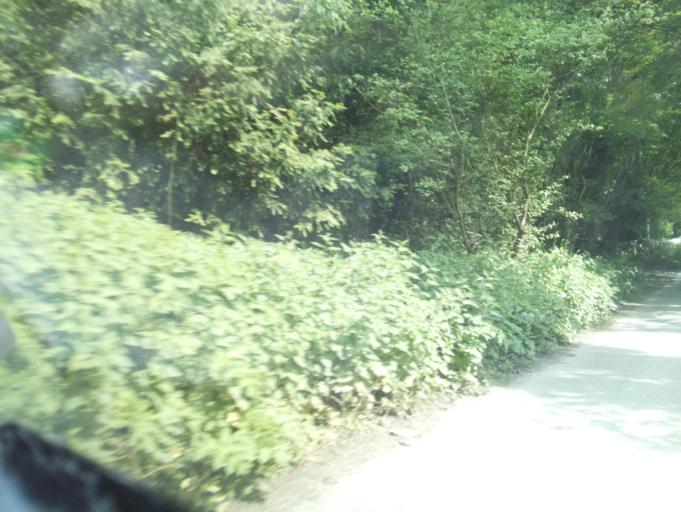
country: GB
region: England
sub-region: South Gloucestershire
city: Horton
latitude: 51.5439
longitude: -2.3498
